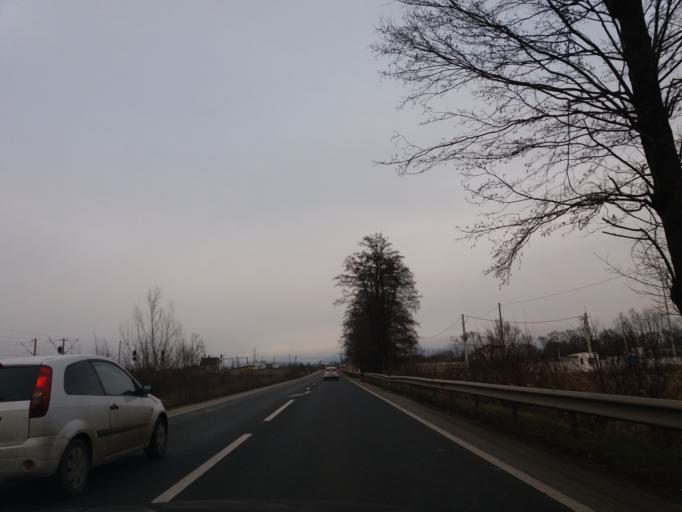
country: RO
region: Hunedoara
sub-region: Comuna Bacia
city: Bacia
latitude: 45.7928
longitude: 23.0014
